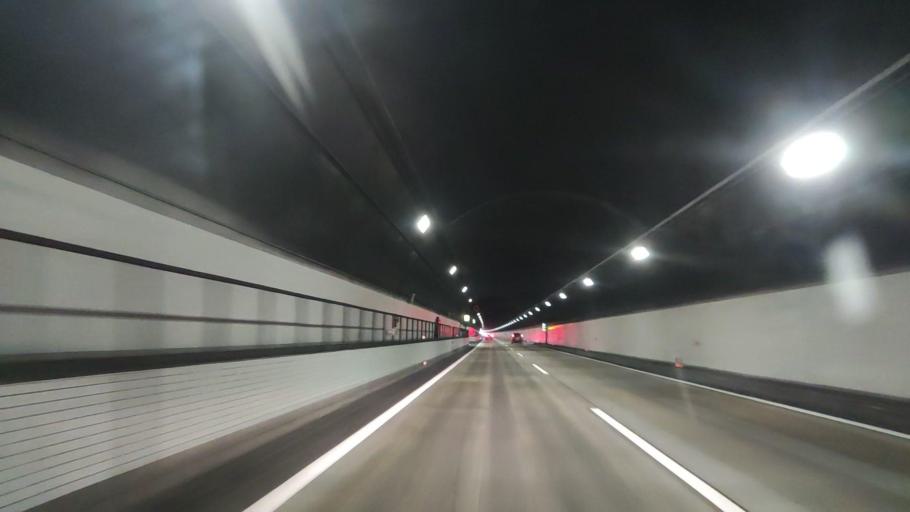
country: JP
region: Hiroshima
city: Fukuyama
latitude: 34.4779
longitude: 133.2980
